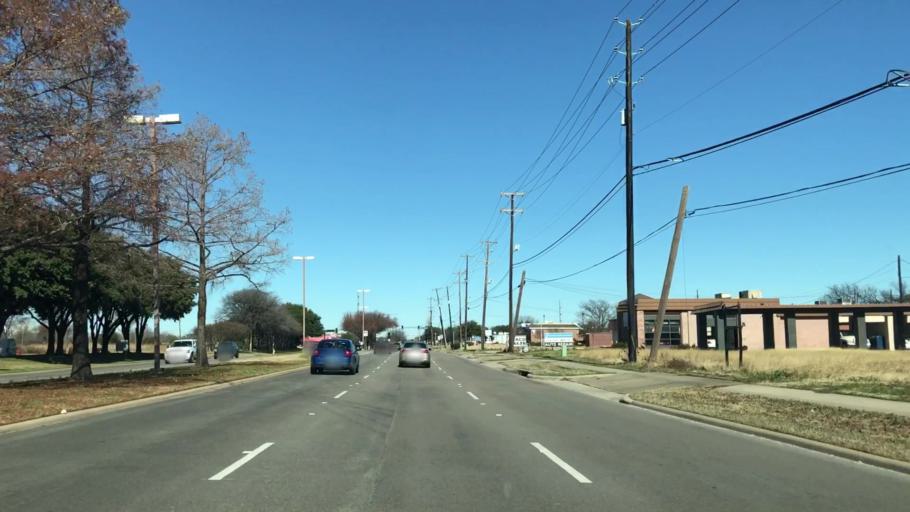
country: US
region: Texas
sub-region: Dallas County
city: Coppell
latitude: 32.9454
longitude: -96.9934
